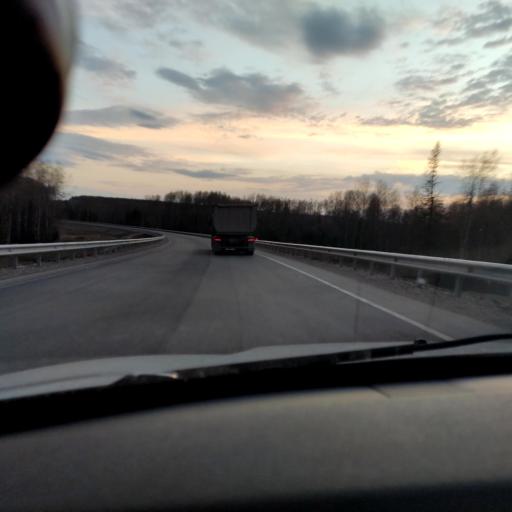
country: RU
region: Perm
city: Chusovoy
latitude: 58.3299
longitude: 57.7674
